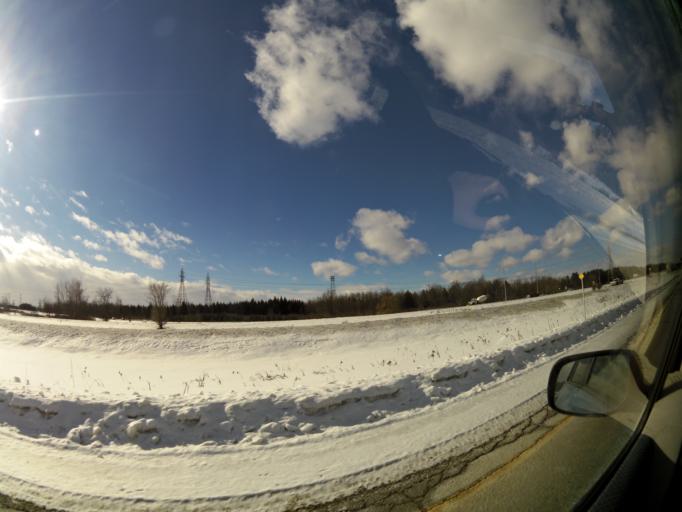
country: CA
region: Ontario
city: Ottawa
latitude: 45.4007
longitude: -75.5928
